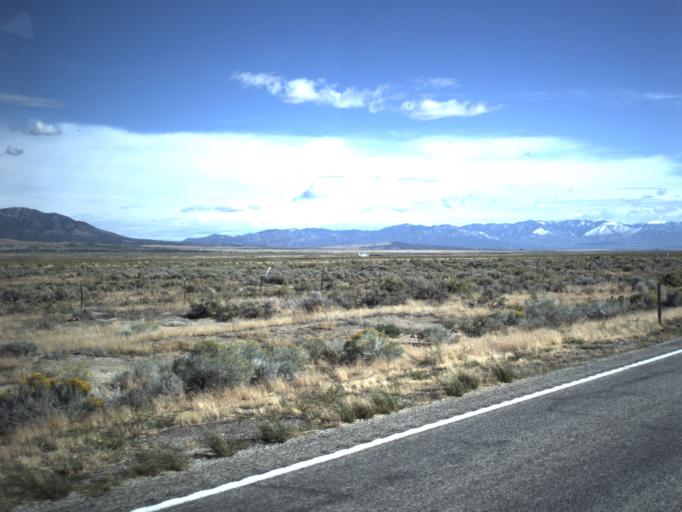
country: US
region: Utah
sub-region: Millard County
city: Delta
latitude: 39.2984
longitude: -112.4706
